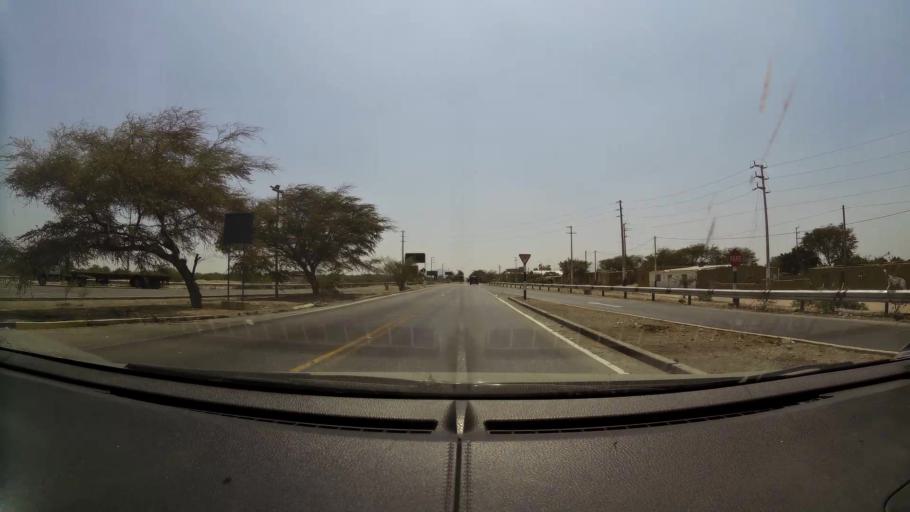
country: PE
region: Lambayeque
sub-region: Provincia de Chiclayo
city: Mocupe
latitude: -7.0194
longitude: -79.6038
